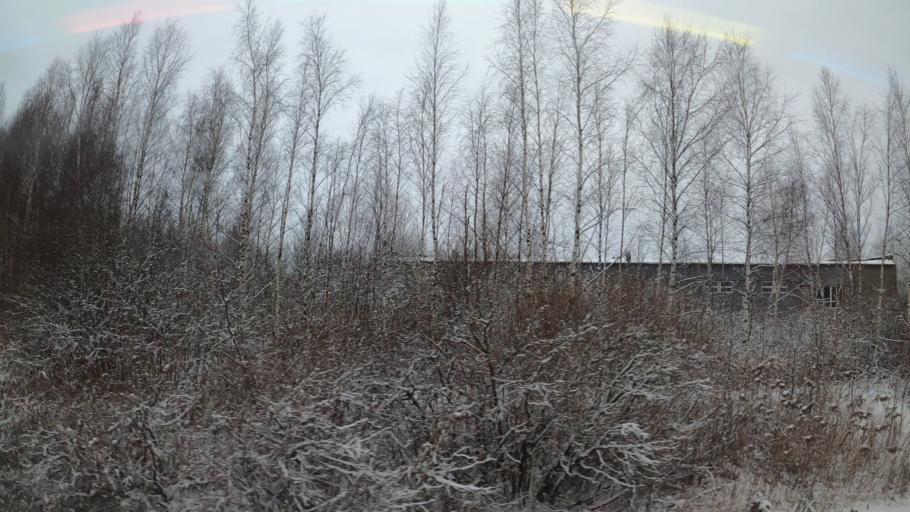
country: RU
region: Jaroslavl
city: Pereslavl'-Zalesskiy
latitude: 56.7247
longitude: 38.9047
